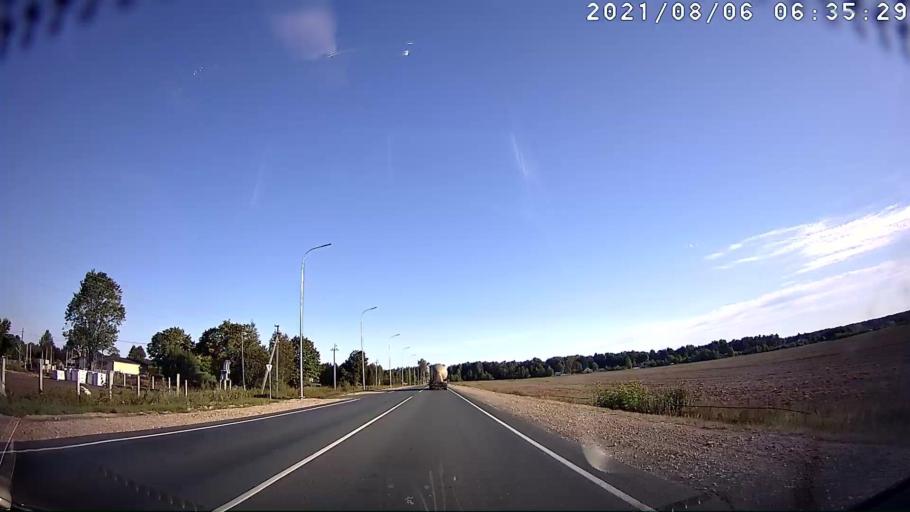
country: RU
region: Mariy-El
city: Suslonger
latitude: 56.2194
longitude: 48.2360
